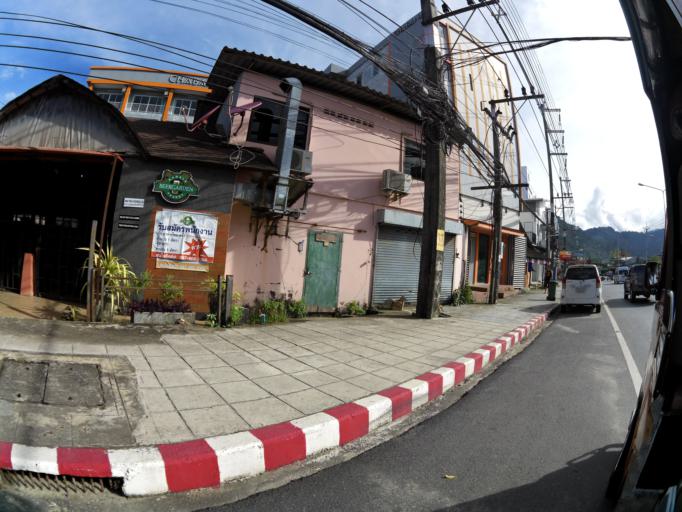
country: TH
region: Phuket
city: Patong
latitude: 7.9485
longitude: 98.2832
